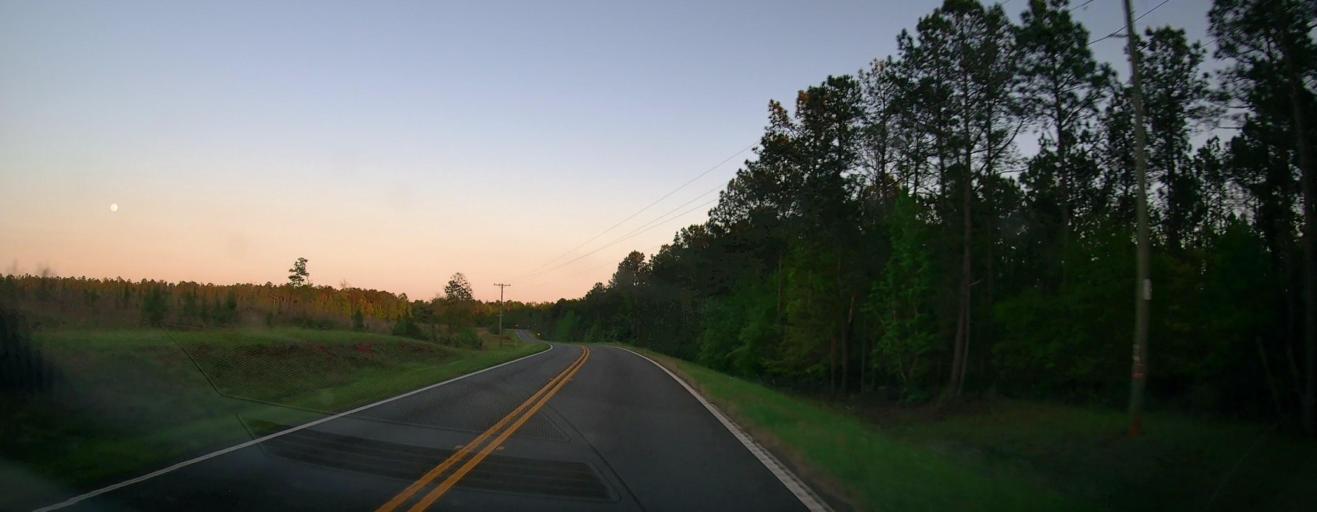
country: US
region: Georgia
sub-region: Marion County
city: Buena Vista
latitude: 32.3822
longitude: -84.5623
